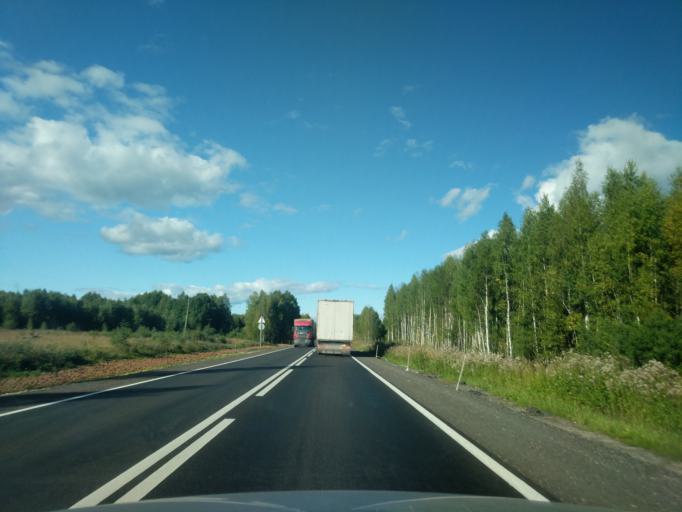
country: RU
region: Kostroma
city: Makar'yev
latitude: 57.9902
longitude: 43.9666
